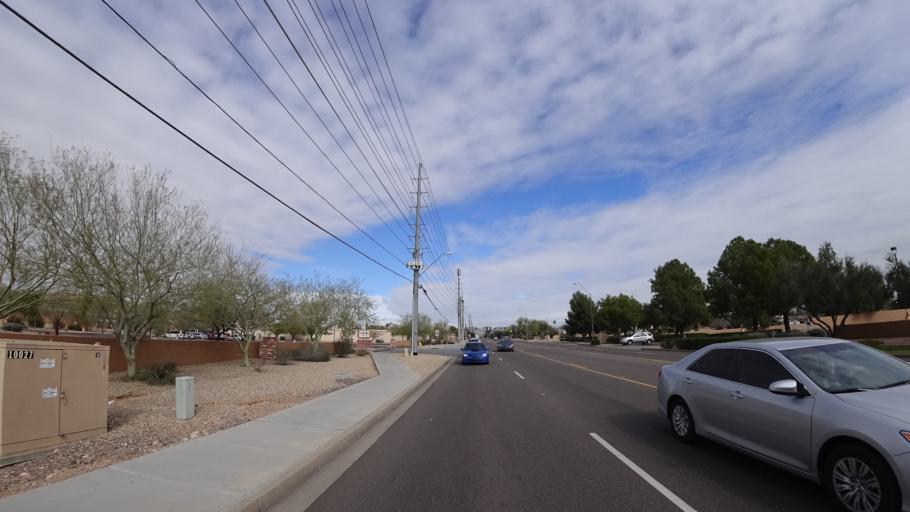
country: US
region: Arizona
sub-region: Maricopa County
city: Peoria
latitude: 33.6418
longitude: -112.1866
